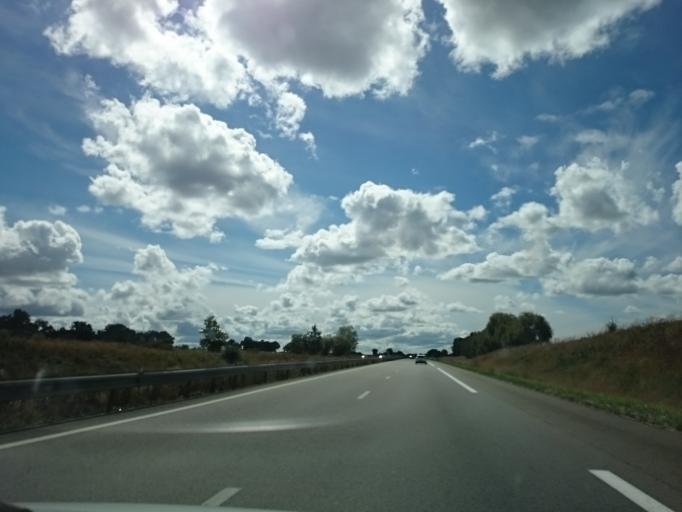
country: FR
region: Pays de la Loire
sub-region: Departement de la Loire-Atlantique
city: Oudon
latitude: 47.3629
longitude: -1.3151
